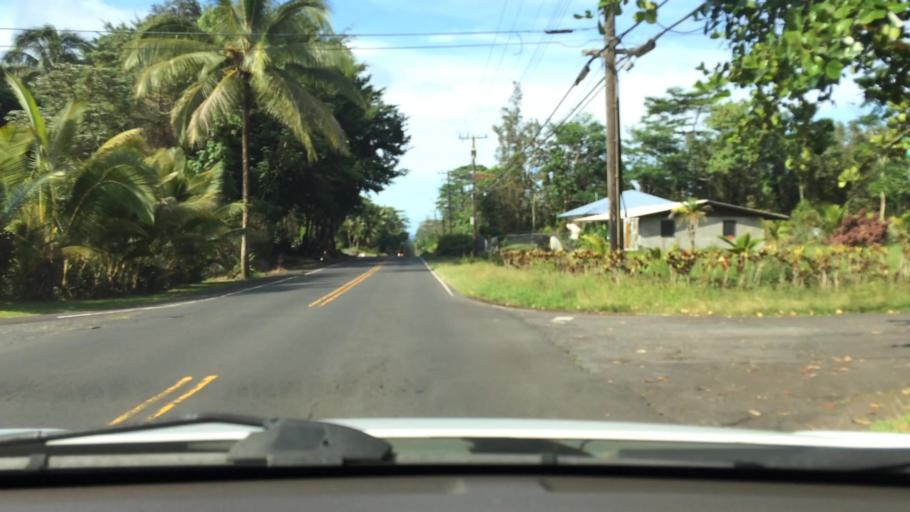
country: US
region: Hawaii
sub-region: Hawaii County
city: Hawaiian Beaches
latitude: 19.5440
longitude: -154.9050
